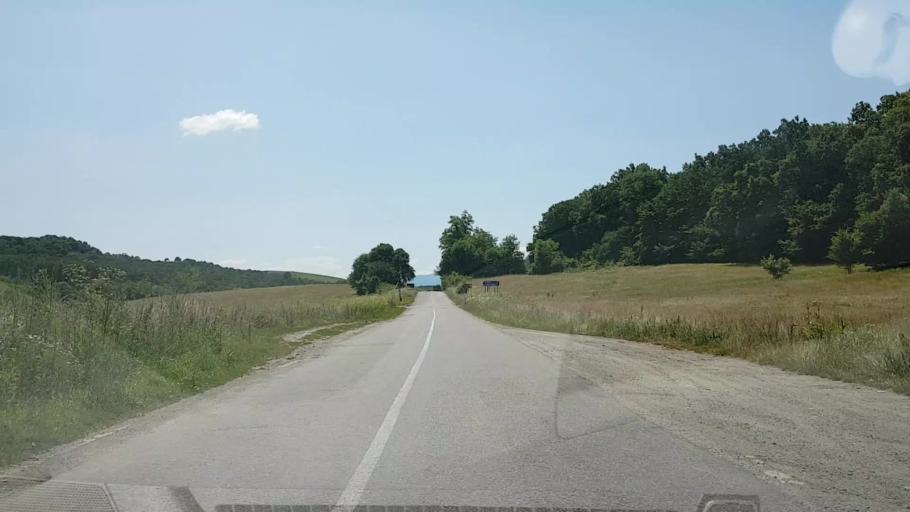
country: RO
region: Brasov
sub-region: Comuna Cincu
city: Cincu
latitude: 45.8708
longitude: 24.8214
